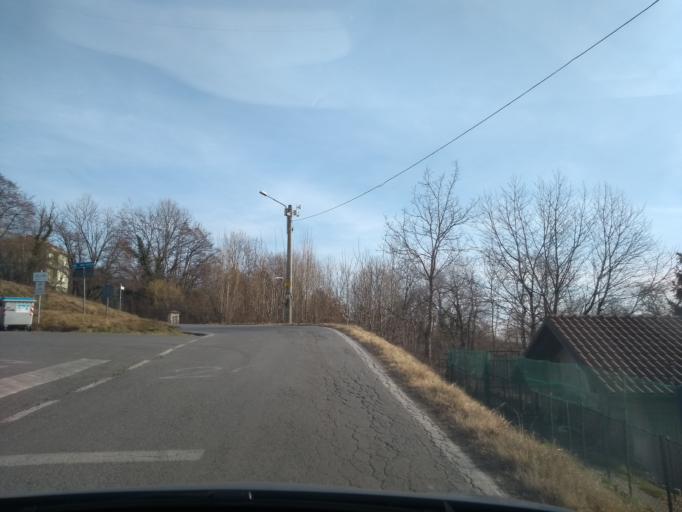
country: IT
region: Piedmont
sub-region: Provincia di Torino
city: Coassolo
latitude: 45.3017
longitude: 7.4810
